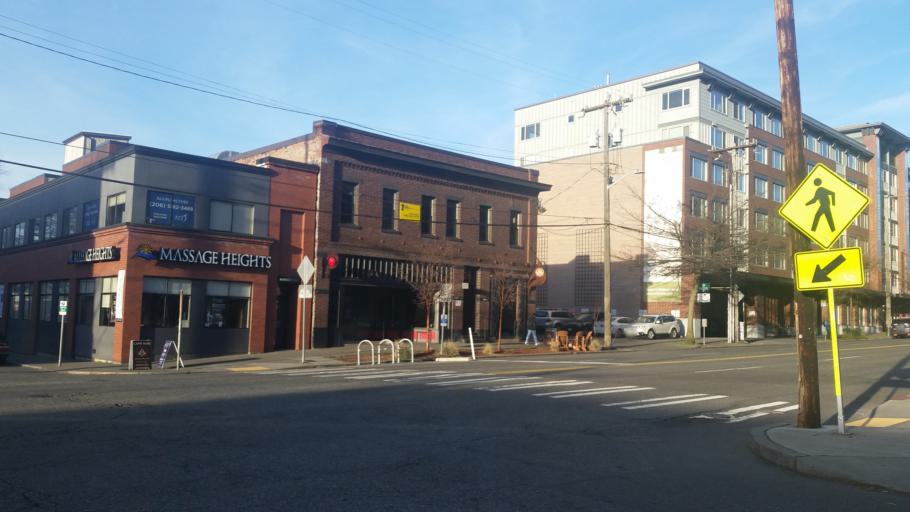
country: US
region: Washington
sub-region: King County
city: Seattle
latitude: 47.6669
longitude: -122.3823
